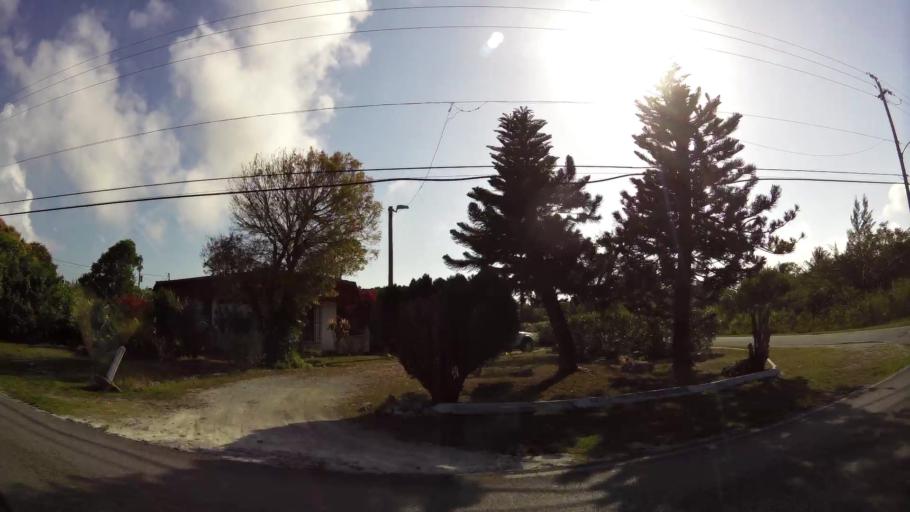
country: BS
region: Freeport
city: Lucaya
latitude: 26.5103
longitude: -78.6600
